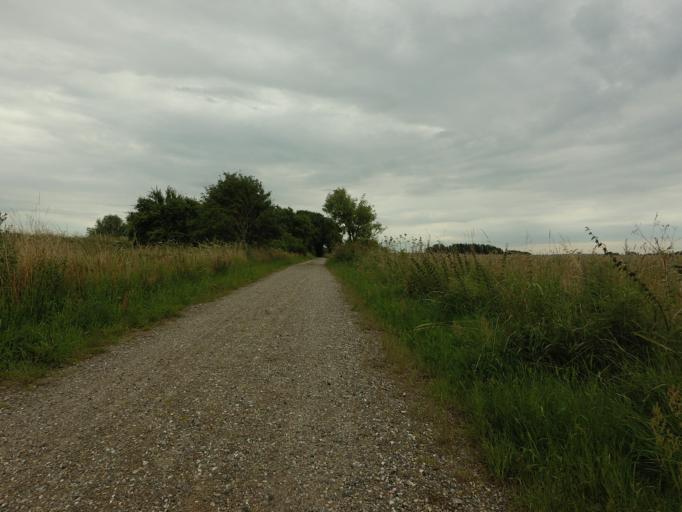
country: DK
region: North Denmark
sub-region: Alborg Kommune
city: Vadum
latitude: 57.1114
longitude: 9.8836
